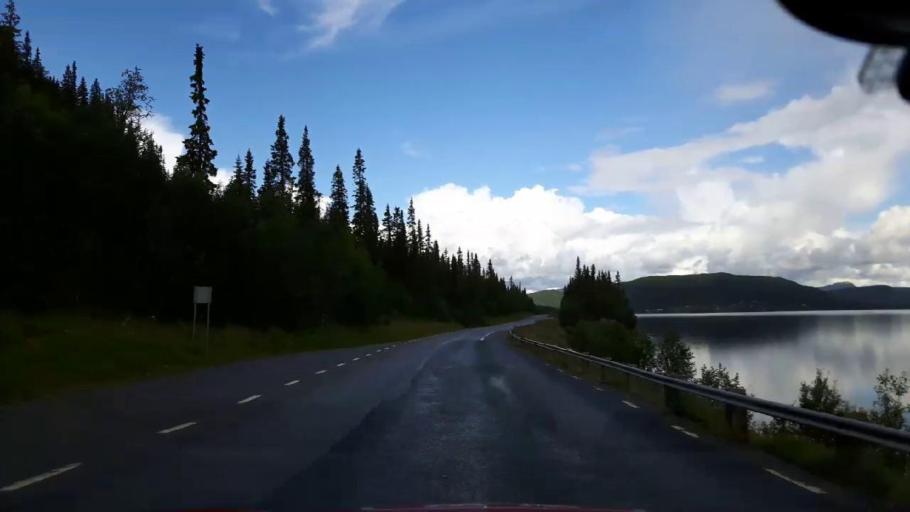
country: SE
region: Vaesterbotten
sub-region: Vilhelmina Kommun
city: Sjoberg
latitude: 65.0020
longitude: 15.1952
